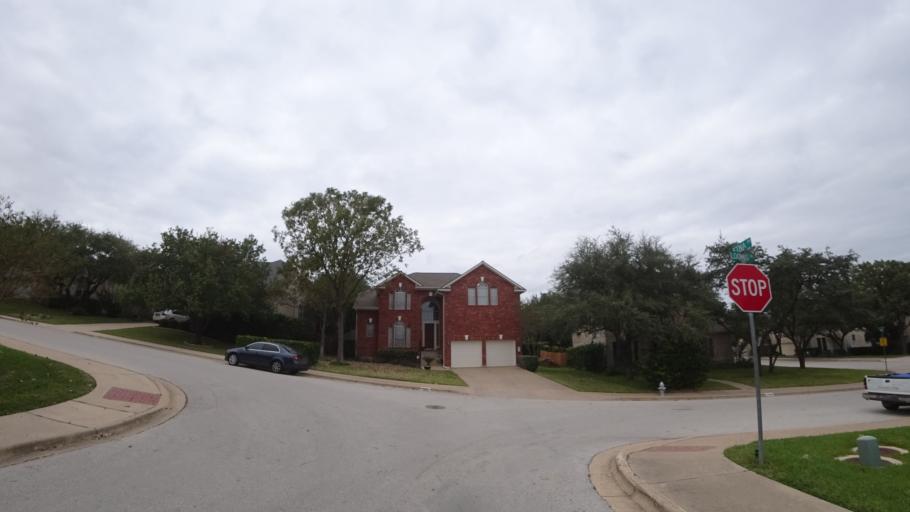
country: US
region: Texas
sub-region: Travis County
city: Bee Cave
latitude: 30.3118
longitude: -97.9215
